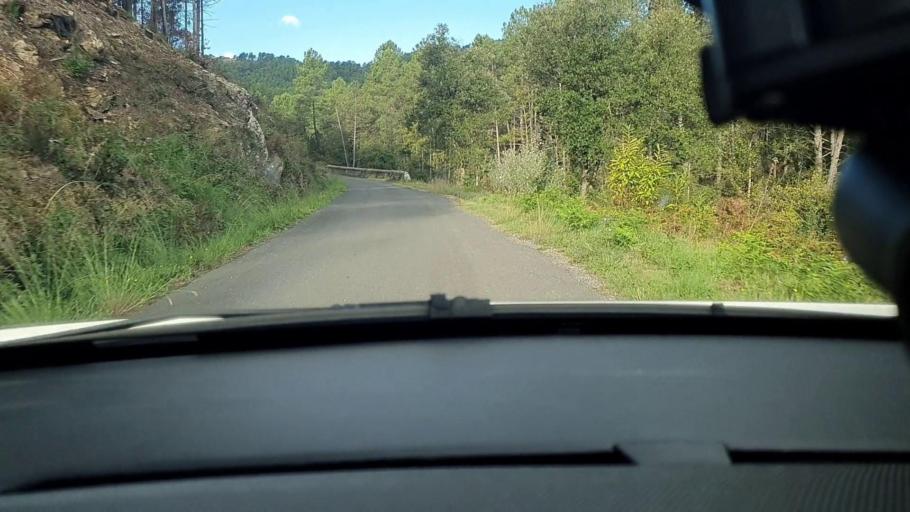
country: FR
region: Languedoc-Roussillon
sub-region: Departement du Gard
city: Besseges
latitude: 44.3306
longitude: 4.0887
